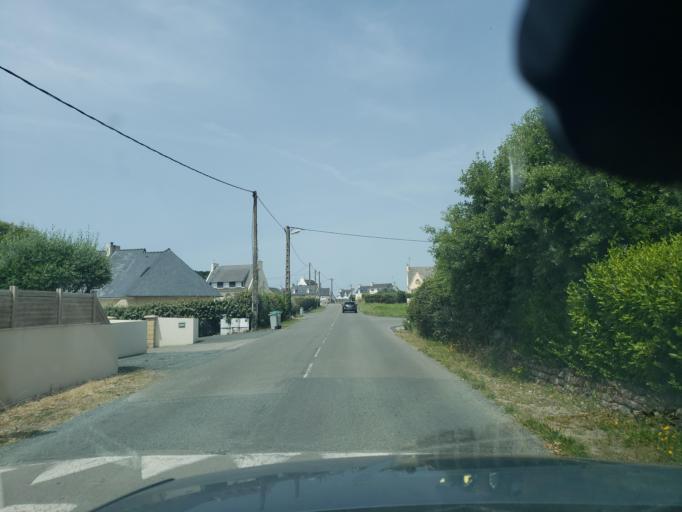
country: FR
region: Brittany
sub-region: Departement du Finistere
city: Guilvinec
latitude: 47.8050
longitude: -4.3039
